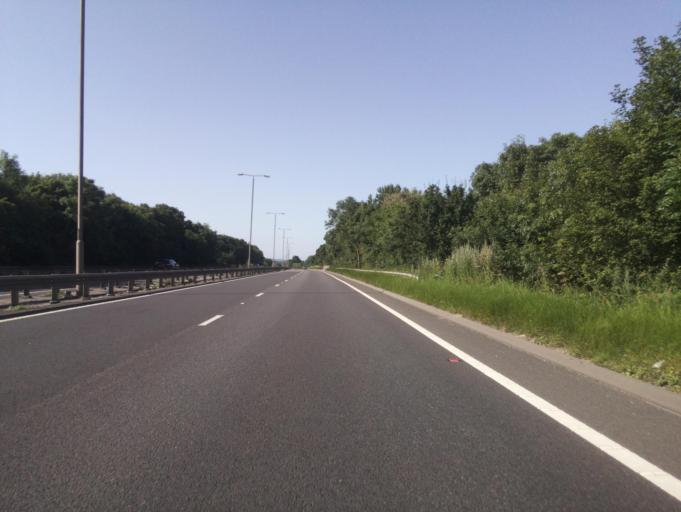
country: GB
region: England
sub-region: Derbyshire
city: Findern
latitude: 52.8975
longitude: -1.5389
